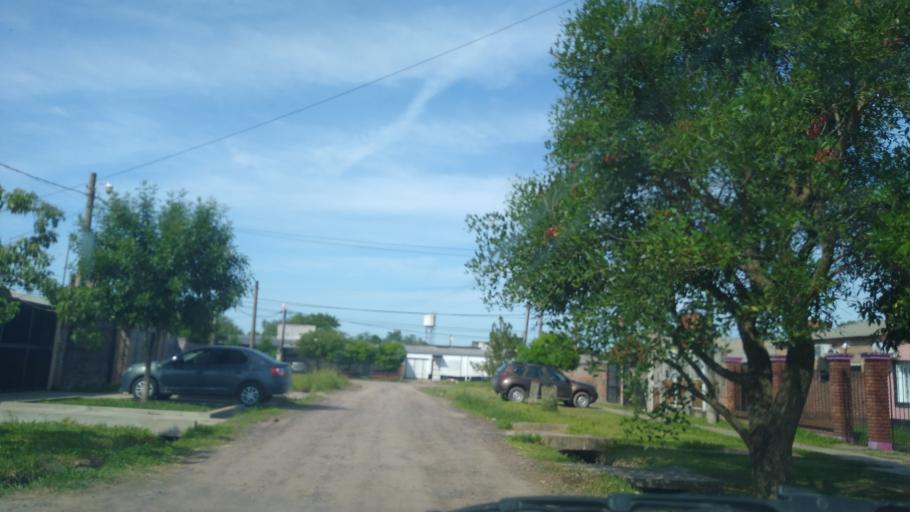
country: AR
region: Chaco
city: Puerto Vilelas
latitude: -27.4977
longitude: -58.9613
